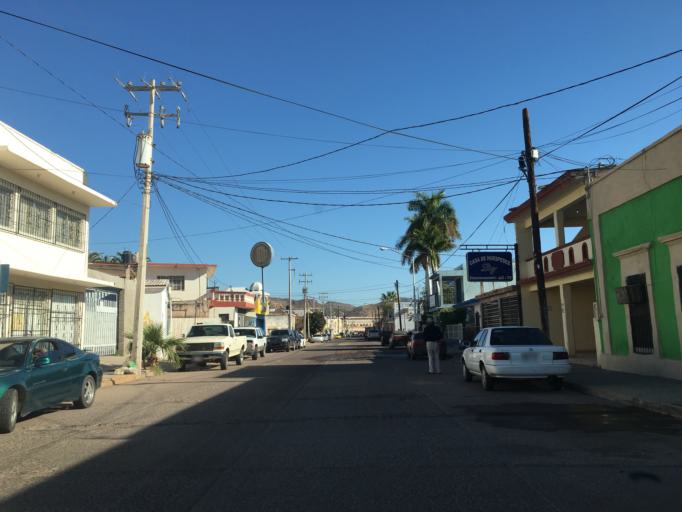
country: MX
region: Sonora
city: Heroica Guaymas
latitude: 27.9197
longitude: -110.8941
